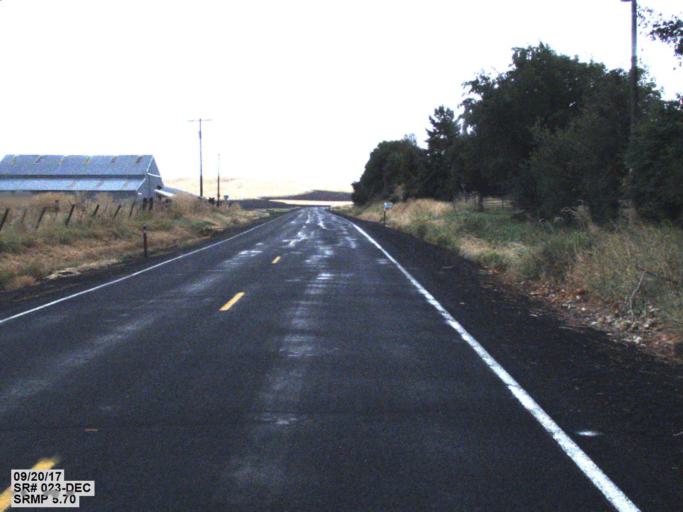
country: US
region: Washington
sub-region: Whitman County
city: Colfax
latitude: 47.0100
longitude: -117.4691
